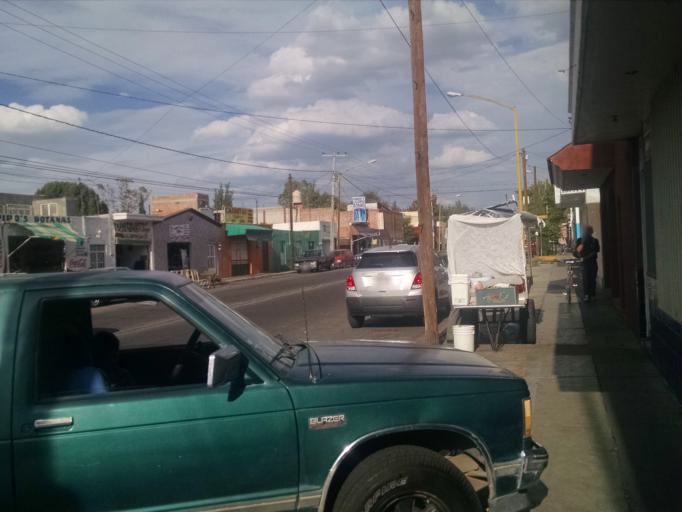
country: MX
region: Aguascalientes
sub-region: Aguascalientes
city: Aguascalientes
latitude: 21.8852
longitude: -102.3106
